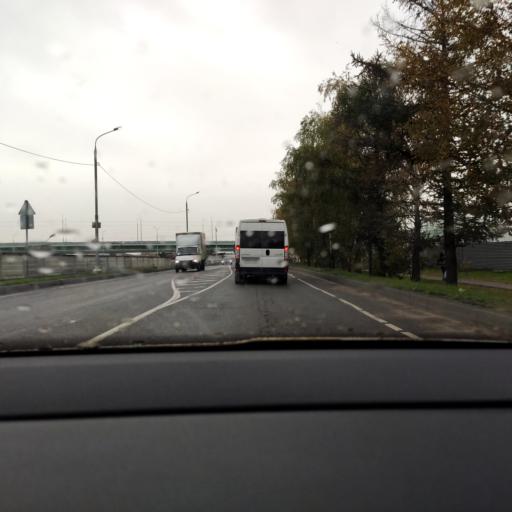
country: RU
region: Moskovskaya
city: Lesnyye Polyany
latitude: 55.9785
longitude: 37.8650
